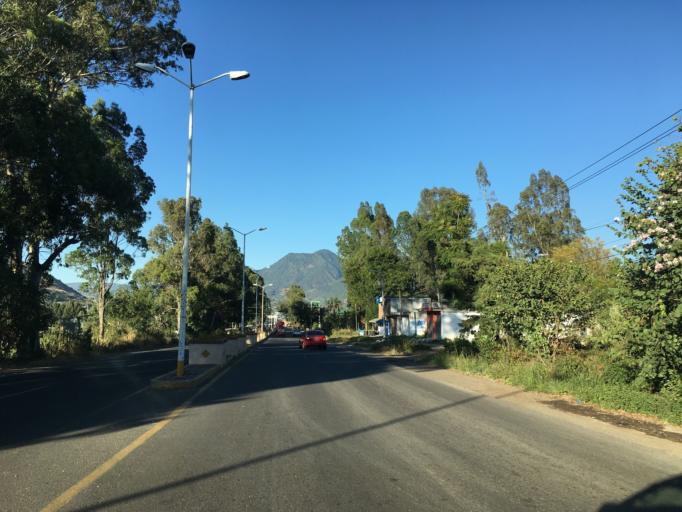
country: MX
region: Michoacan
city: Tuxpan
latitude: 19.5516
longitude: -100.4716
